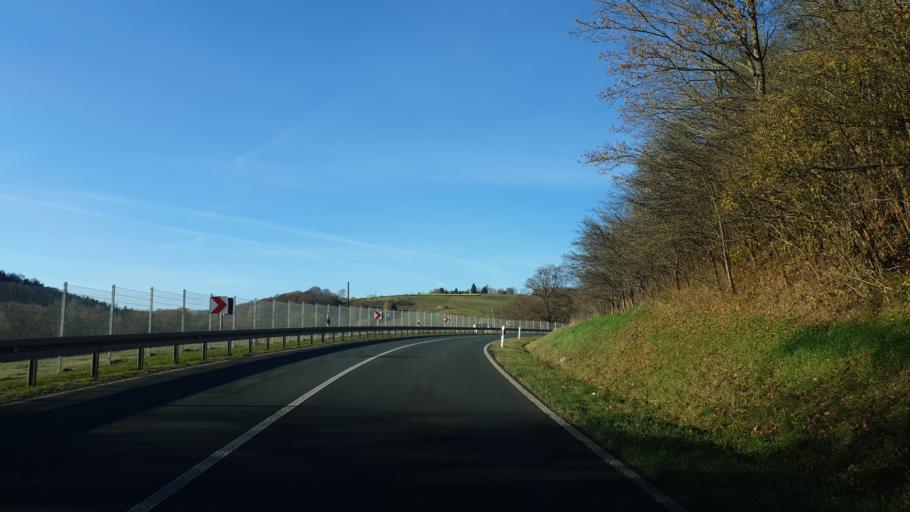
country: DE
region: Thuringia
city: Rauda
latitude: 50.9529
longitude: 11.9304
